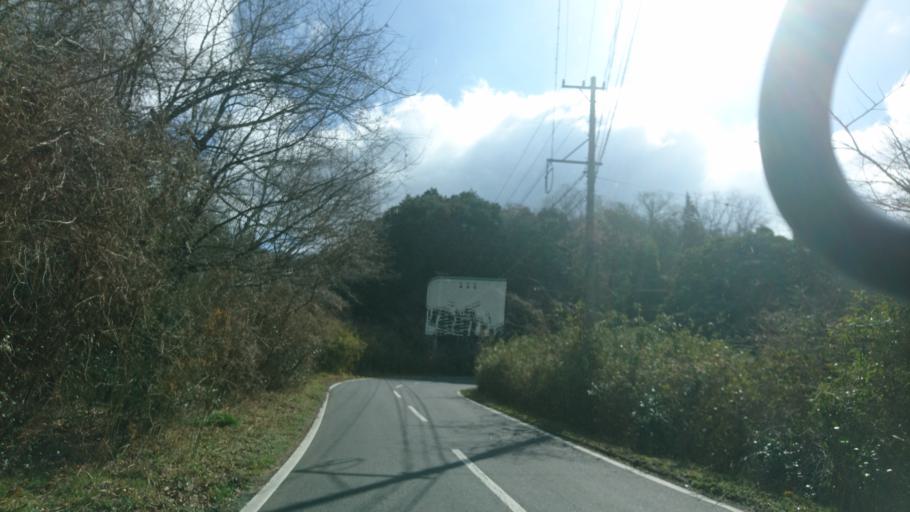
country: JP
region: Mie
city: Ueno-ebisumachi
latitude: 34.7462
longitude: 136.0539
